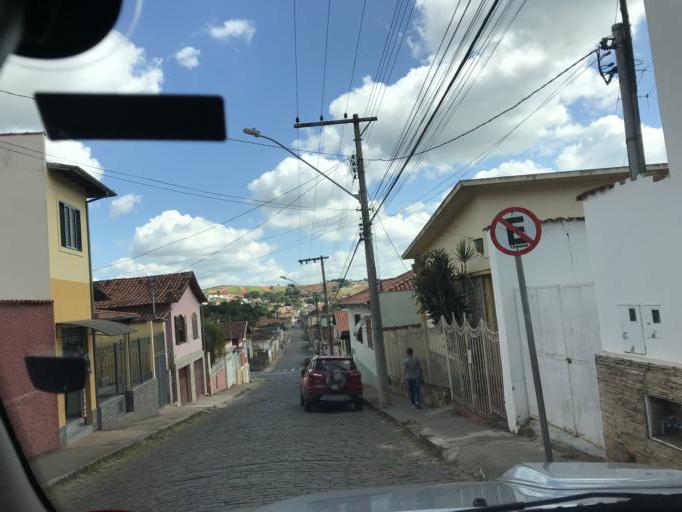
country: BR
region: Minas Gerais
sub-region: Campanha
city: Campanha
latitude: -21.8334
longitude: -45.4018
